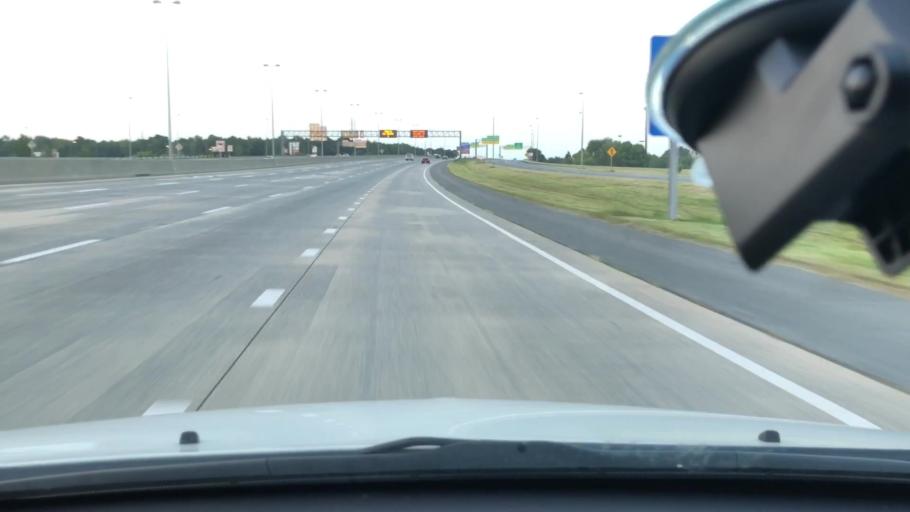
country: US
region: Virginia
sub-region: City of Chesapeake
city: Chesapeake
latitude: 36.7741
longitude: -76.2536
